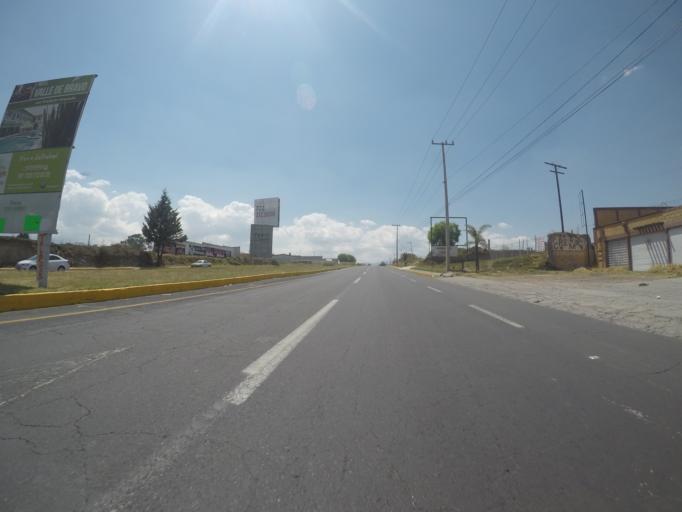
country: MX
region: Mexico
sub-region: Toluca
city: San Antonio Buenavista
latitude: 19.2564
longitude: -99.7100
